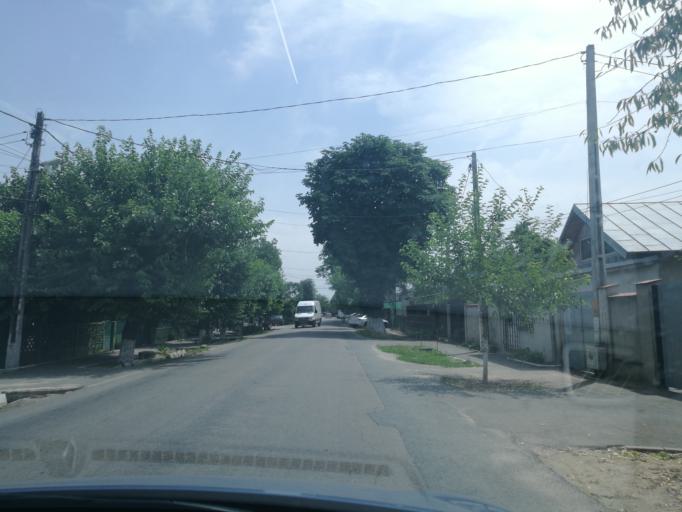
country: RO
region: Ilfov
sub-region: Comuna Jilava
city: Jilava
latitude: 44.3271
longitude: 26.0827
